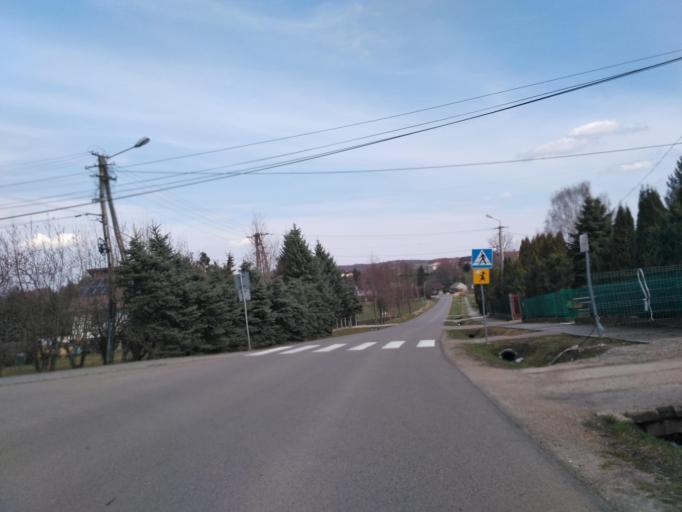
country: PL
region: Subcarpathian Voivodeship
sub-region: Powiat ropczycko-sedziszowski
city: Iwierzyce
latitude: 50.0179
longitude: 21.7855
